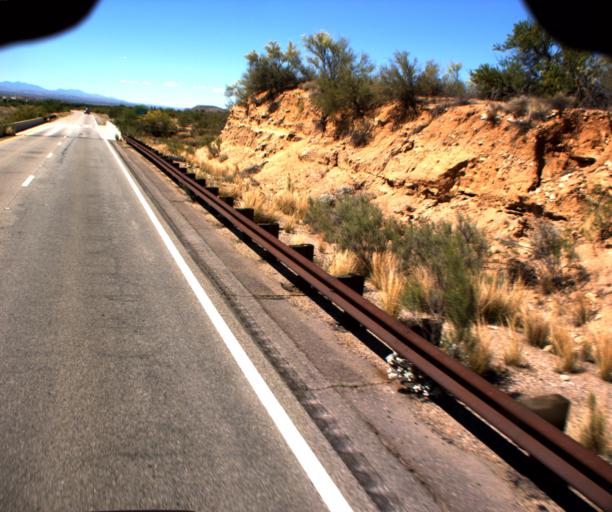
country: US
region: Arizona
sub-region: Yavapai County
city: Bagdad
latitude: 34.6552
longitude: -113.5747
